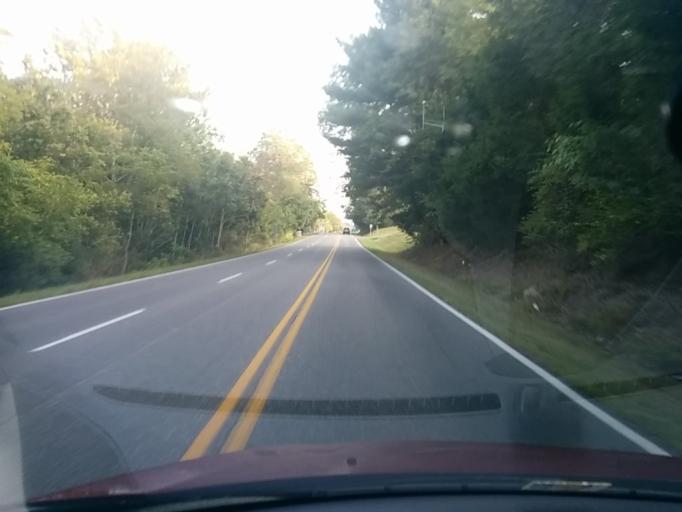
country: US
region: Virginia
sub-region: City of Lexington
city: Lexington
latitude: 37.7662
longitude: -79.4471
